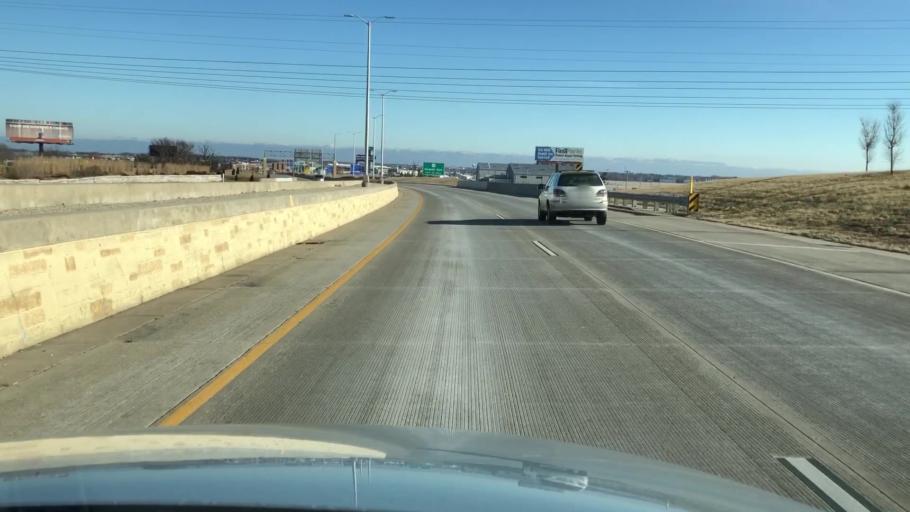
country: US
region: Wisconsin
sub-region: Milwaukee County
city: Saint Francis
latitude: 42.9414
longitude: -87.9266
